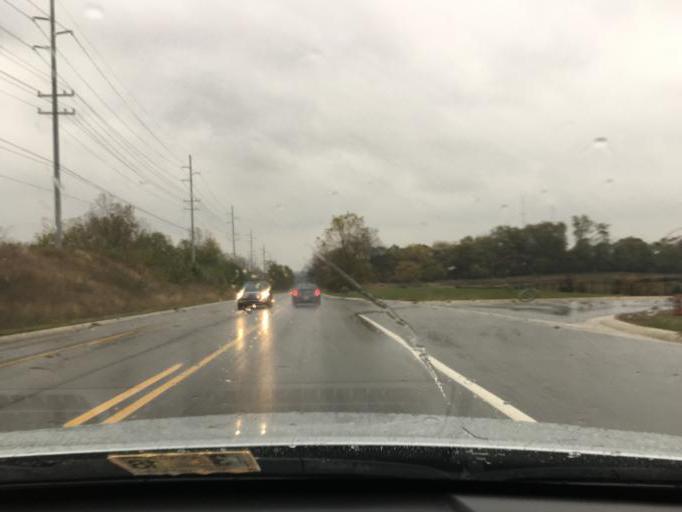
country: US
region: Michigan
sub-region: Oakland County
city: Auburn Hills
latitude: 42.7091
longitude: -83.2285
